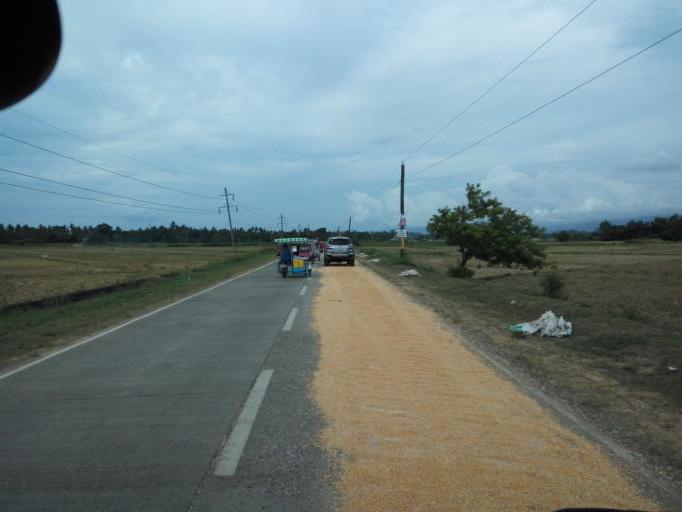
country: PH
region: Cagayan Valley
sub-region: Province of Cagayan
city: Santa Teresita
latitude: 18.2370
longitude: 121.8984
